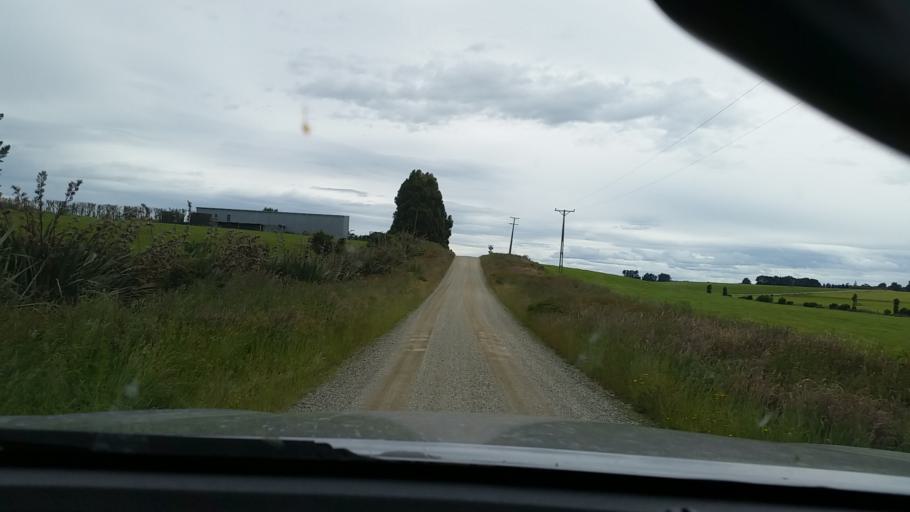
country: NZ
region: Southland
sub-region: Invercargill City
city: Invercargill
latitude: -46.2705
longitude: 168.5268
